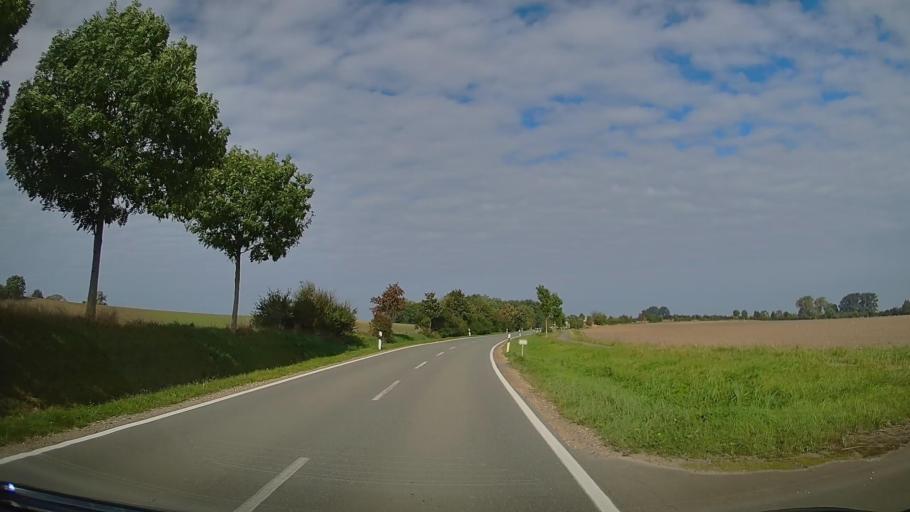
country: DE
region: Schleswig-Holstein
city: Gremersdorf
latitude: 54.3371
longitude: 10.8920
